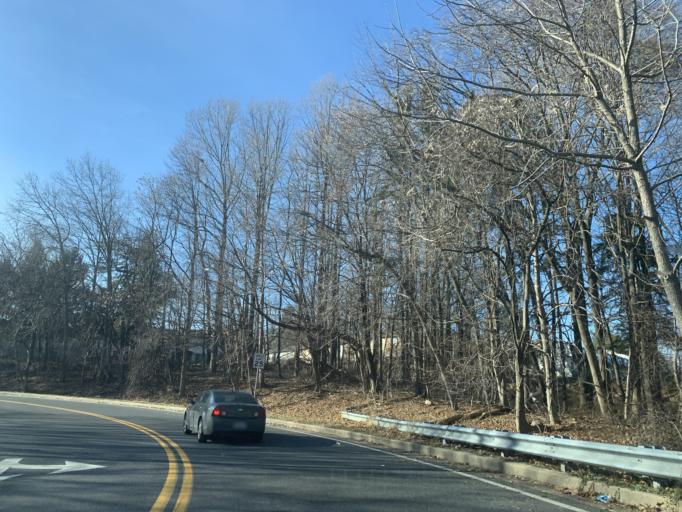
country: US
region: Maryland
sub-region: Baltimore County
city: Owings Mills
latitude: 39.4165
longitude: -76.7836
